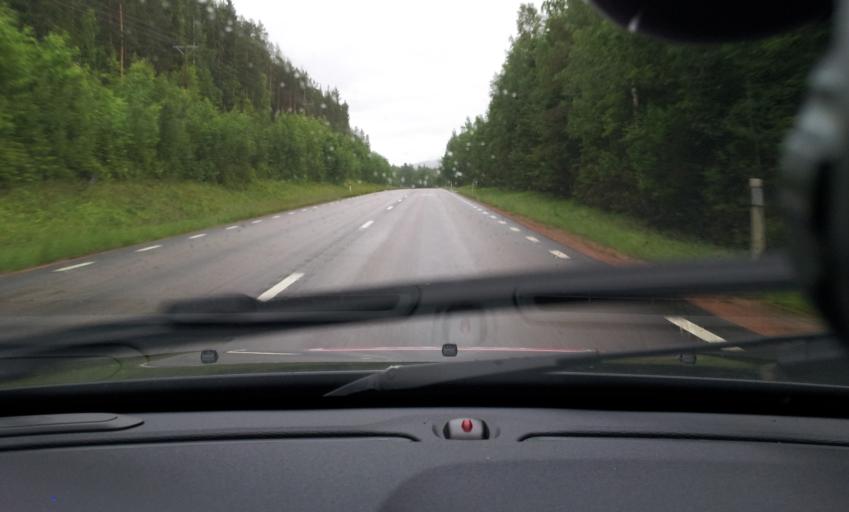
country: SE
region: Jaemtland
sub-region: Ragunda Kommun
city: Hammarstrand
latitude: 63.1581
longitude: 15.9734
